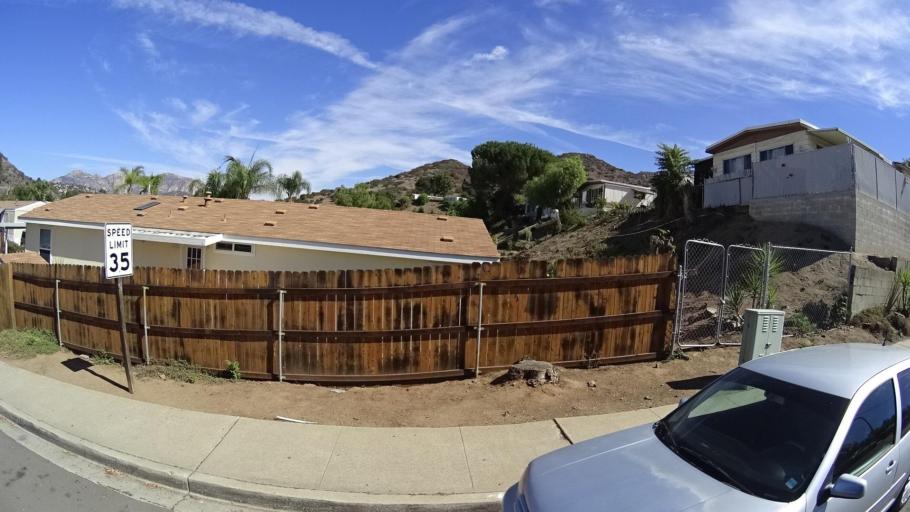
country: US
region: California
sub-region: San Diego County
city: Crest
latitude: 32.8417
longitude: -116.8765
